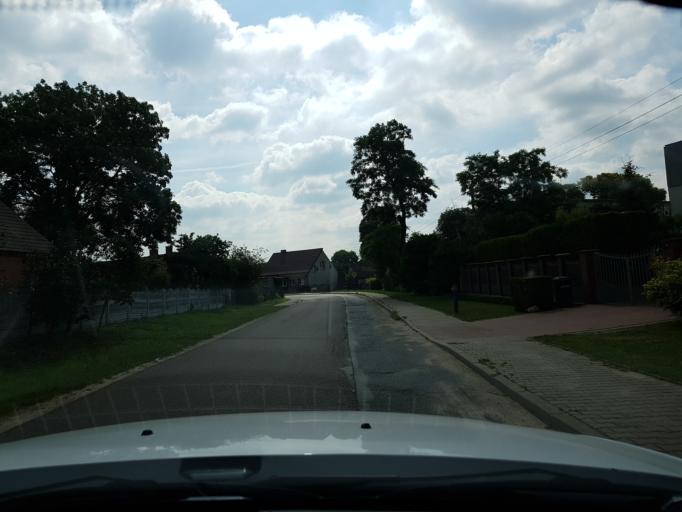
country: PL
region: West Pomeranian Voivodeship
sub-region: Powiat gryfinski
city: Banie
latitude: 53.1282
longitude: 14.6066
